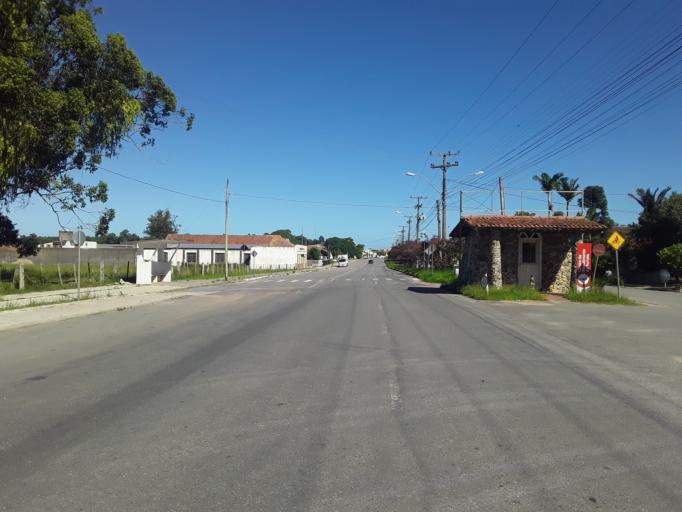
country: BR
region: Rio Grande do Sul
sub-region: Sao Lourenco Do Sul
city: Sao Lourenco do Sul
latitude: -31.3490
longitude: -51.9919
